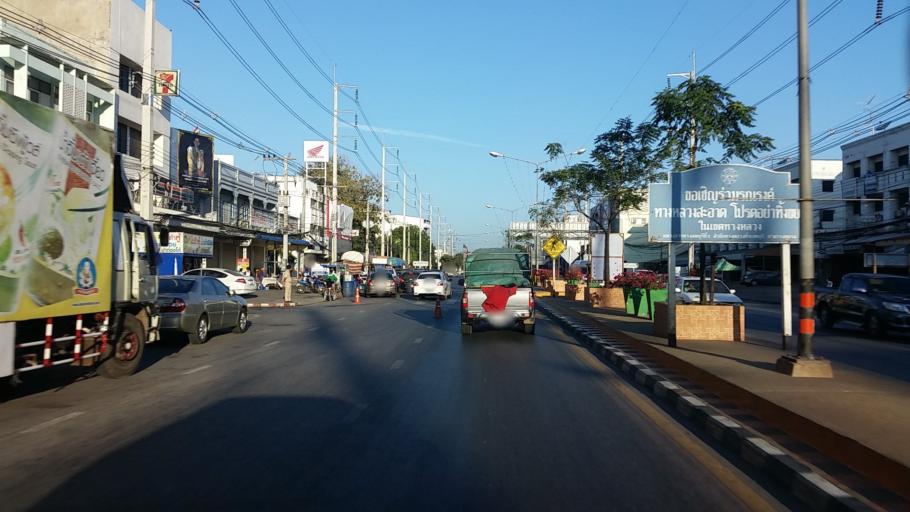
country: TH
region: Lop Buri
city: Chai Badan
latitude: 15.2078
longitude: 101.1333
